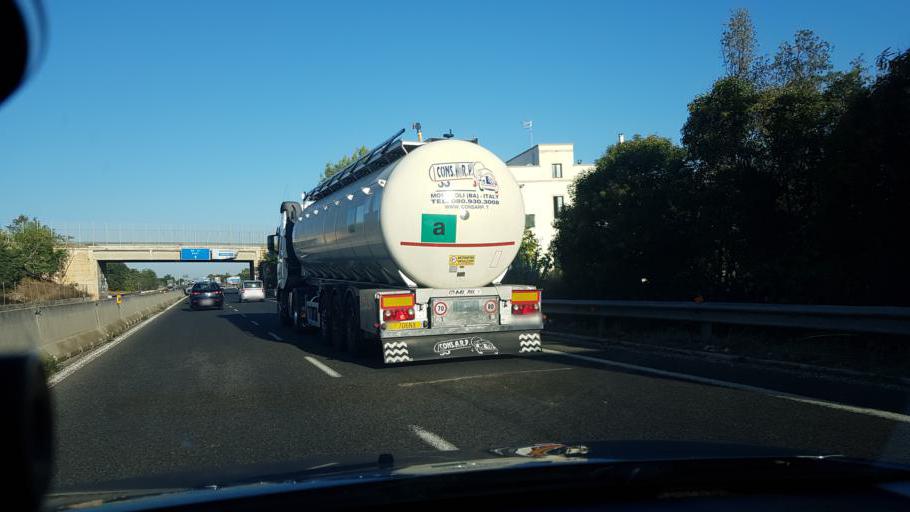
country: IT
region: Apulia
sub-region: Provincia di Bari
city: Monopoli
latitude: 40.9349
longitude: 17.2938
